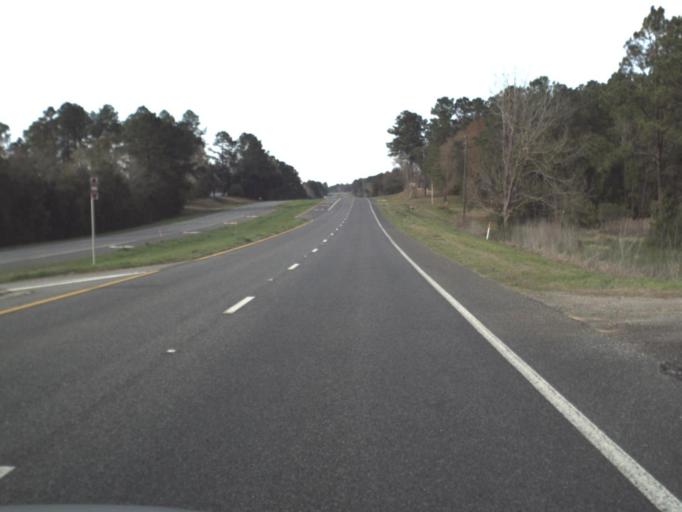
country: US
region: Florida
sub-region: Jefferson County
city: Monticello
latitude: 30.5683
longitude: -83.8698
